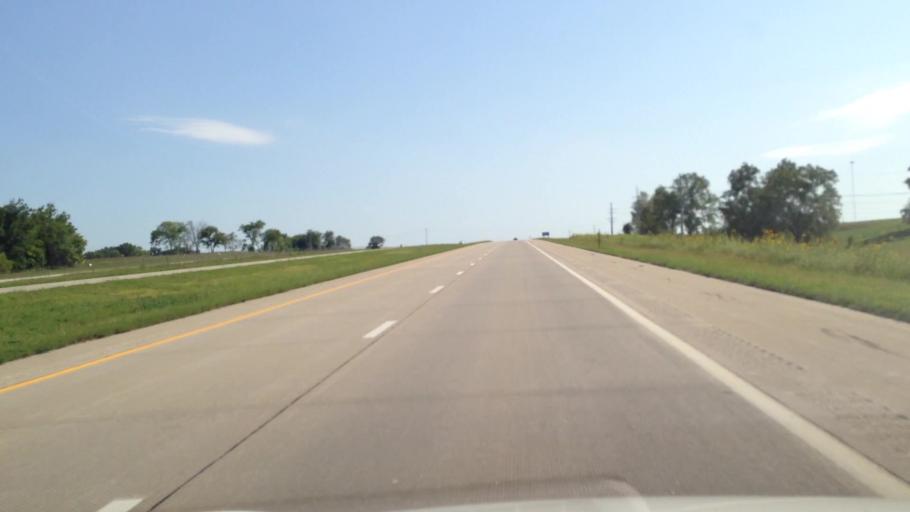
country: US
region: Kansas
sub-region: Linn County
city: Pleasanton
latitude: 38.2006
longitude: -94.7056
